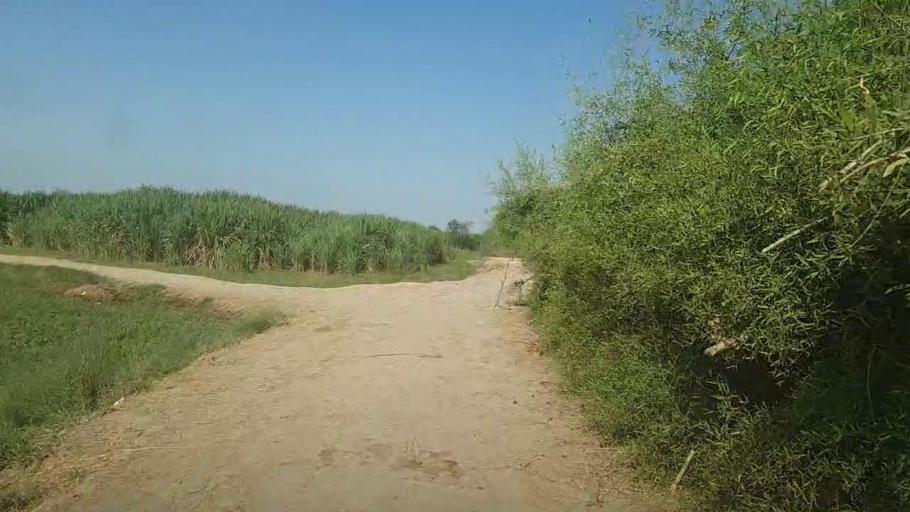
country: PK
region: Sindh
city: Khairpur
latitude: 28.1255
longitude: 69.6188
